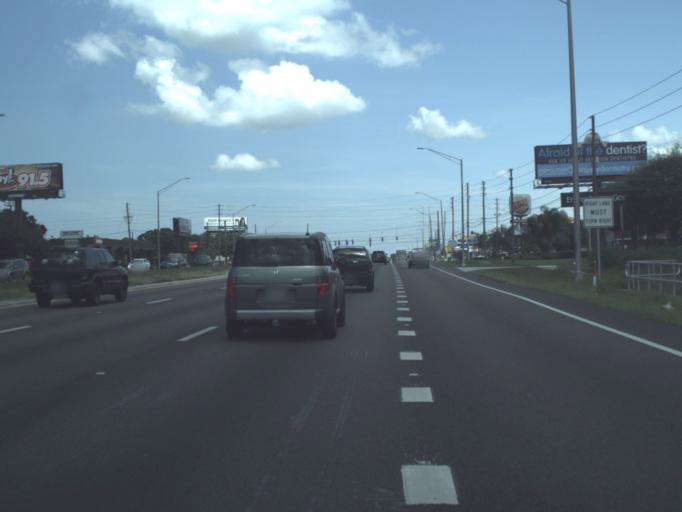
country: US
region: Florida
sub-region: Pinellas County
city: Saint George
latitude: 28.0648
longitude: -82.7387
